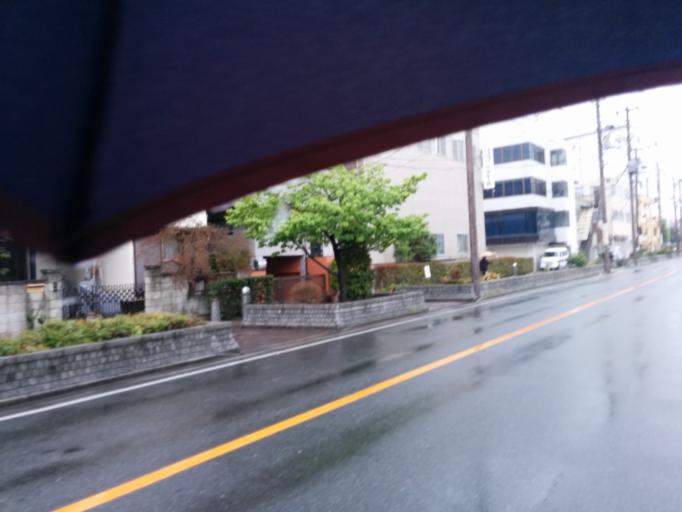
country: JP
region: Saitama
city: Shimotoda
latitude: 35.8193
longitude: 139.6772
